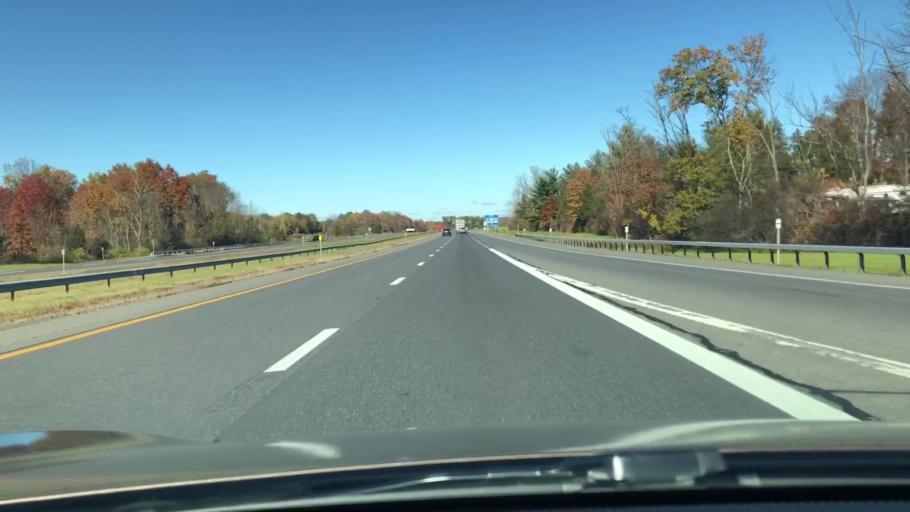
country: US
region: New York
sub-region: Ulster County
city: Saugerties South
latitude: 42.0566
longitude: -73.9829
